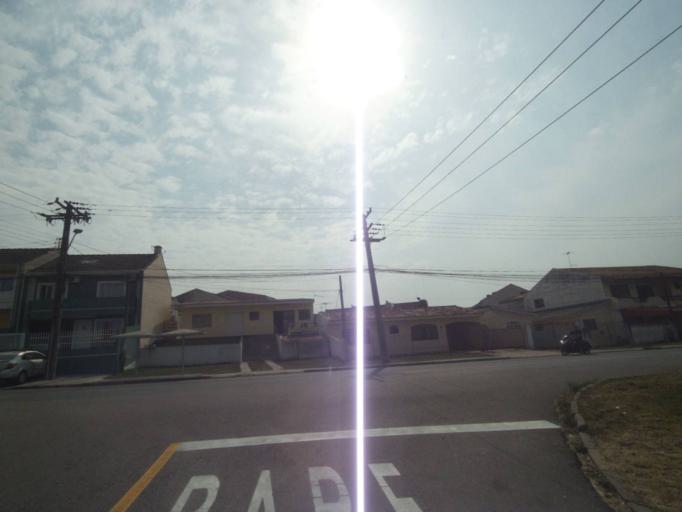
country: BR
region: Parana
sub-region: Pinhais
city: Pinhais
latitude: -25.4819
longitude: -49.2099
